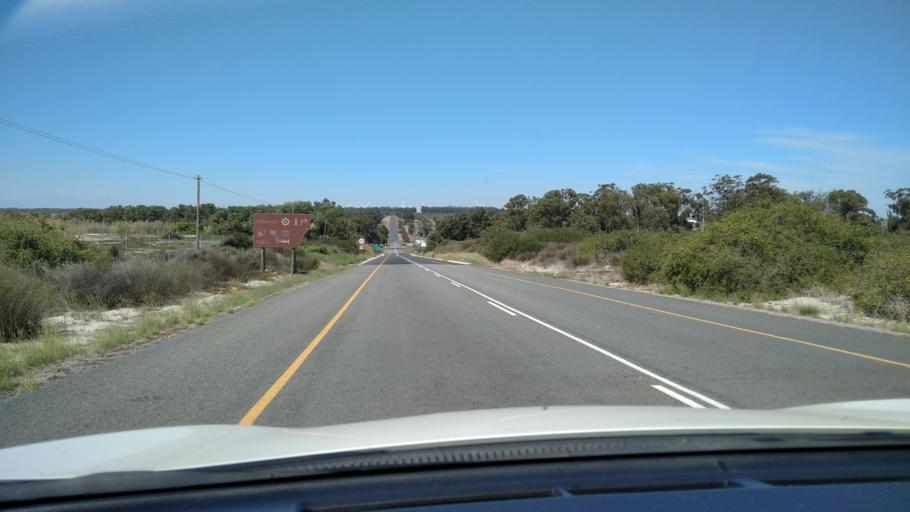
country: ZA
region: Western Cape
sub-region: West Coast District Municipality
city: Moorreesburg
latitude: -33.0535
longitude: 18.3382
